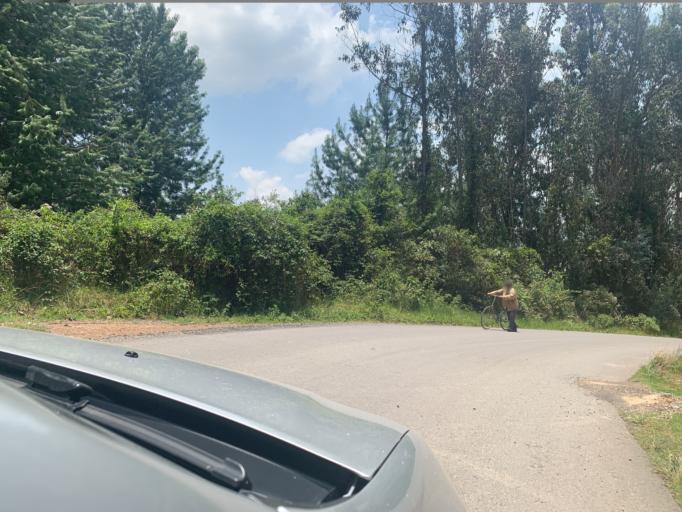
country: CO
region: Boyaca
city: Chiquinquira
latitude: 5.5362
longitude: -73.7441
